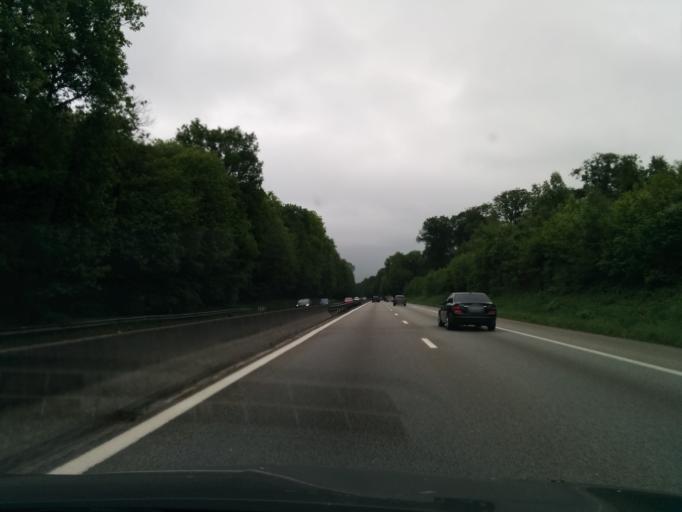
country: FR
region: Ile-de-France
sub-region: Departement des Yvelines
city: Saint-Nom-la-Breteche
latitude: 48.8895
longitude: 2.0102
